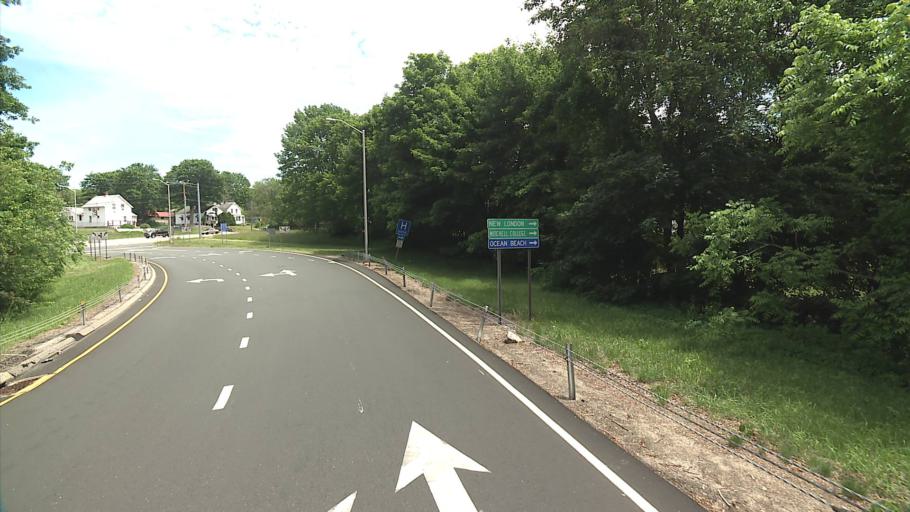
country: US
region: Connecticut
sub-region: New London County
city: Central Waterford
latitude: 41.3696
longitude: -72.1330
